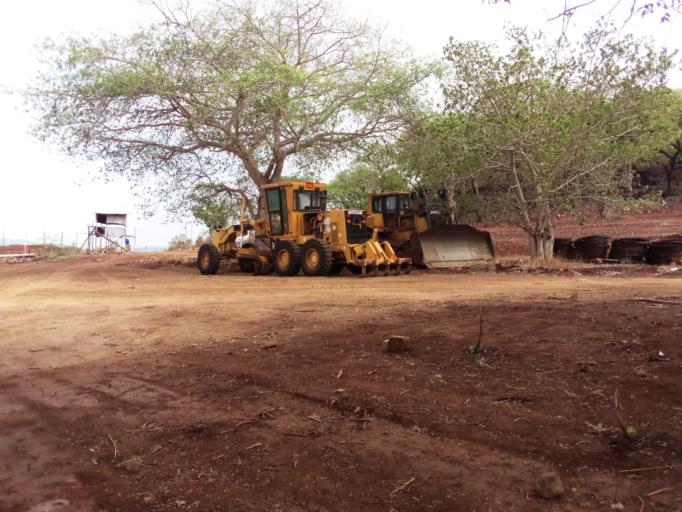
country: ET
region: Oromiya
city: Mendi
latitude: 10.0601
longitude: 35.2822
